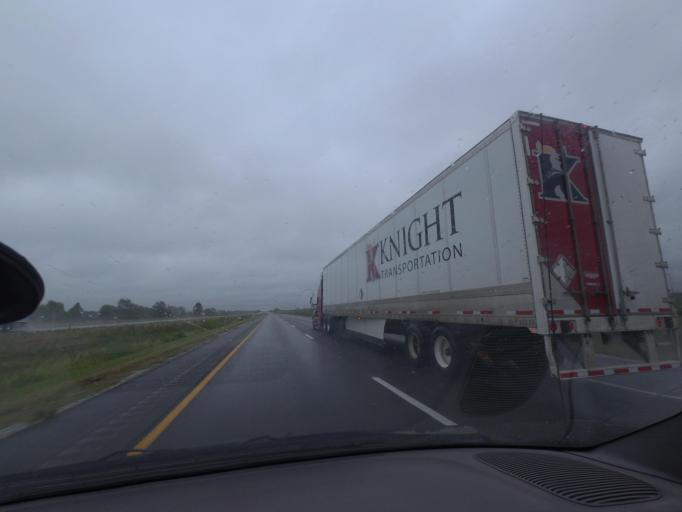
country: US
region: Illinois
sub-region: Scott County
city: Winchester
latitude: 39.6810
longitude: -90.4787
